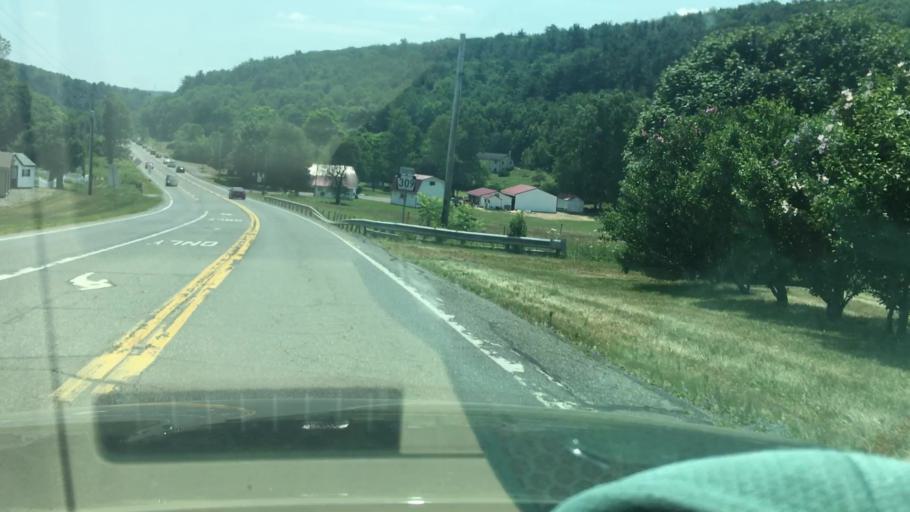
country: US
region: Pennsylvania
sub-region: Schuylkill County
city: Coaldale
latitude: 40.7424
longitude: -75.8920
